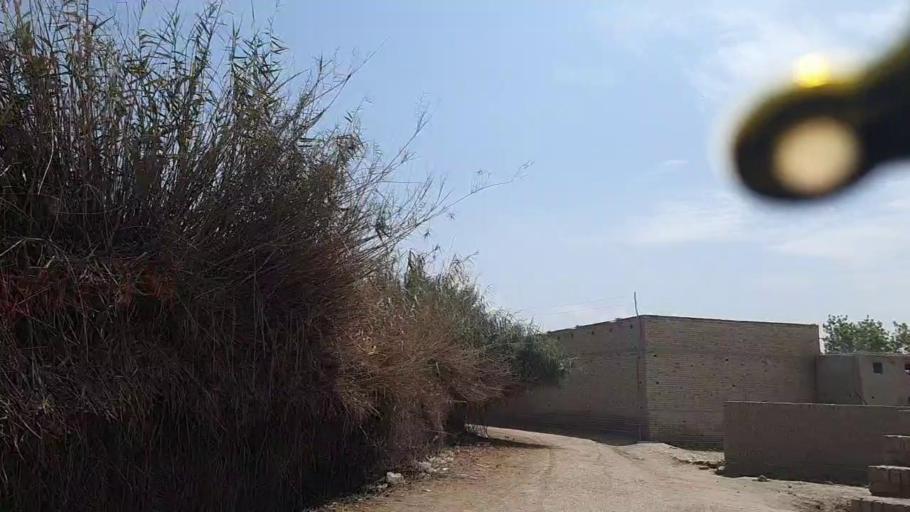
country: PK
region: Sindh
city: Rustam jo Goth
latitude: 28.1083
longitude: 68.8813
